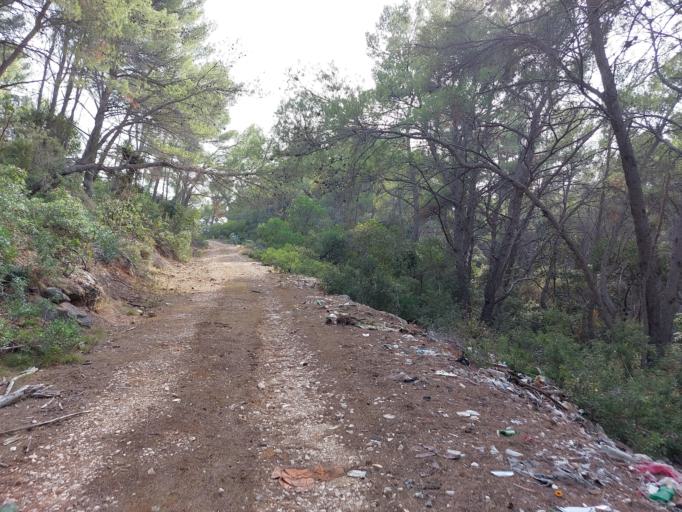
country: HR
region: Dubrovacko-Neretvanska
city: Smokvica
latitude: 42.7348
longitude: 16.8302
